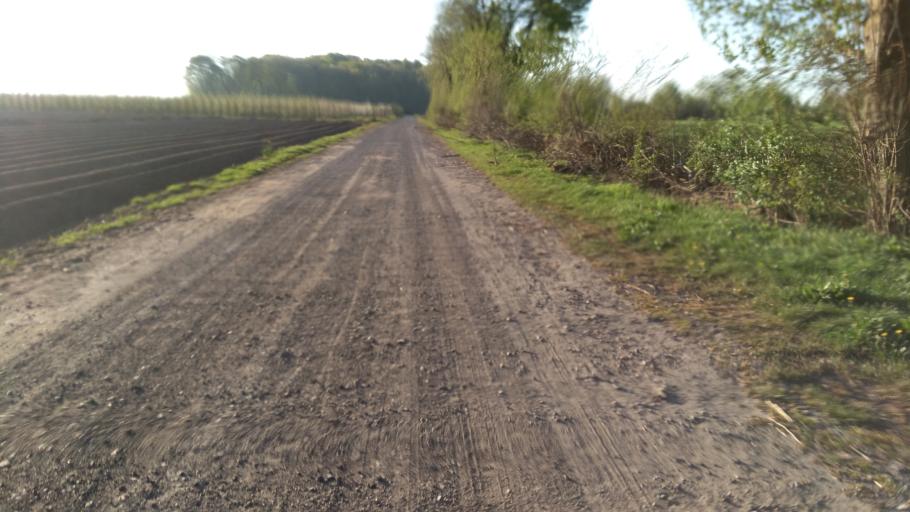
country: DE
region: Lower Saxony
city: Bliedersdorf
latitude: 53.4741
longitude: 9.5803
